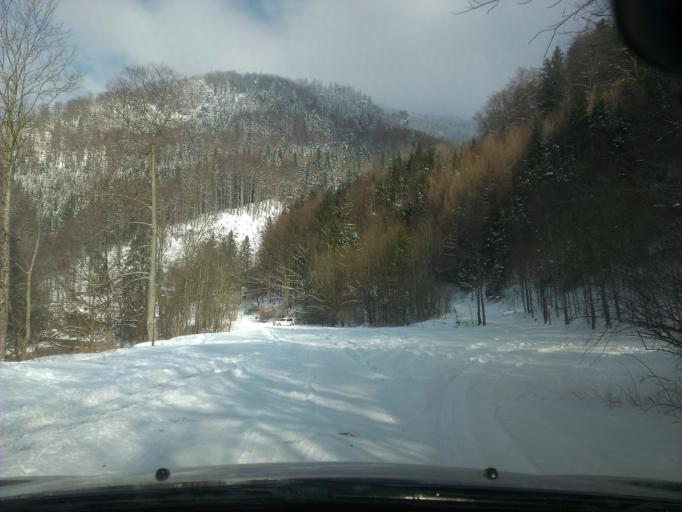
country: AT
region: Lower Austria
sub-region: Politischer Bezirk Neunkirchen
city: Reichenau an der Rax
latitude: 47.7465
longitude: 15.7700
